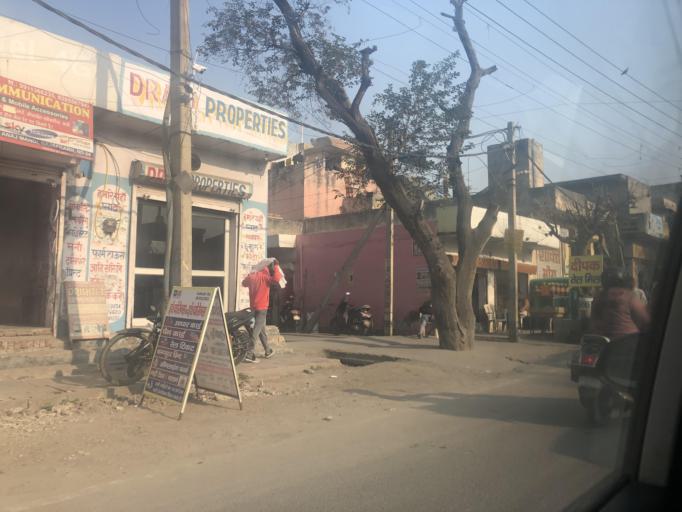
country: IN
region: Haryana
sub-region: Jhajjar
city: Bahadurgarh
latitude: 28.6187
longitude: 76.9748
